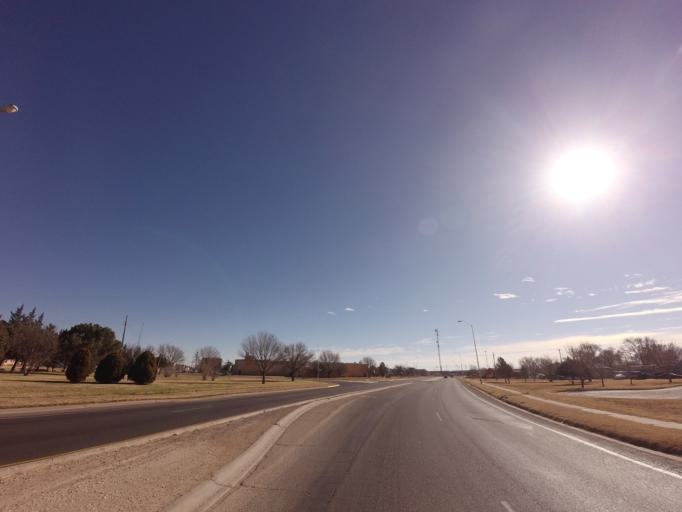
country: US
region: New Mexico
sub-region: Curry County
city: Clovis
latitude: 34.4005
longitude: -103.2118
